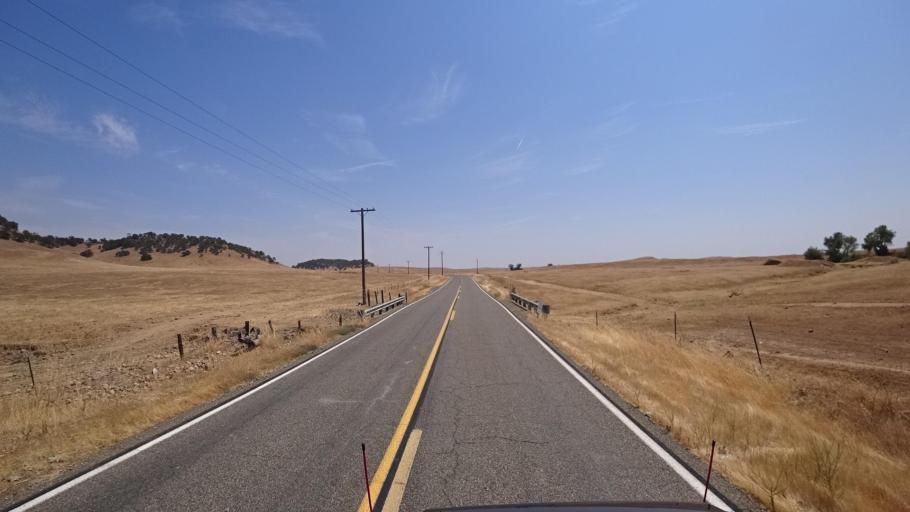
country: US
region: California
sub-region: Merced County
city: Planada
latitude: 37.4985
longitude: -120.3122
